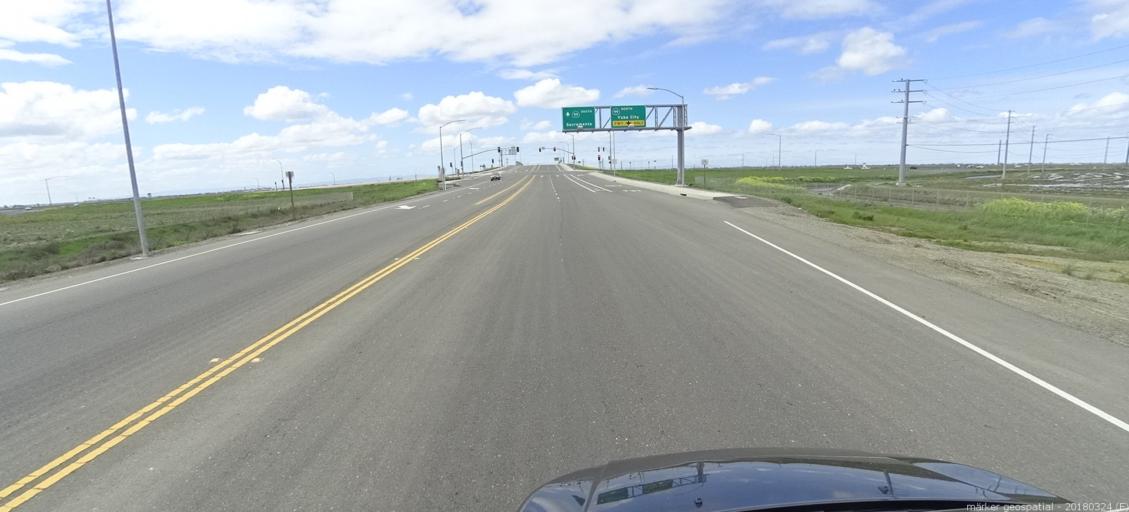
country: US
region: California
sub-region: Sacramento County
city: Elverta
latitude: 38.7143
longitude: -121.5362
